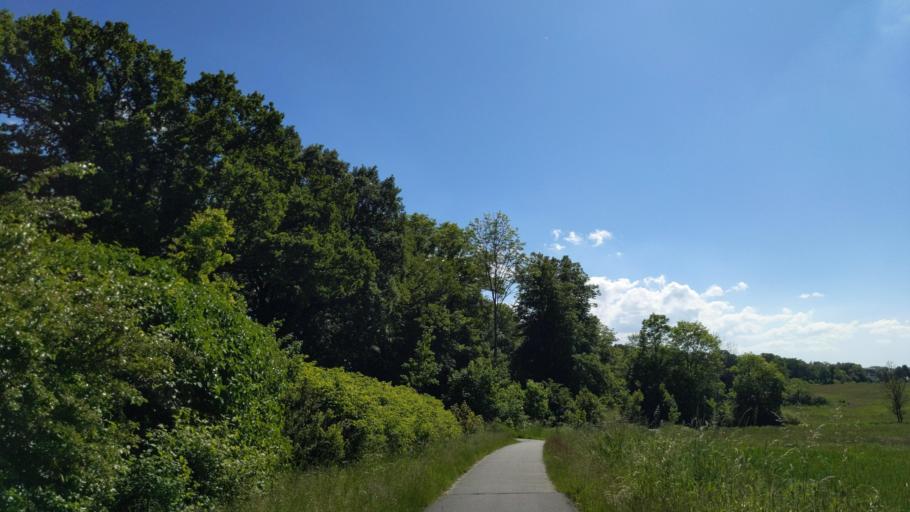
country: DE
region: Schleswig-Holstein
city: Eutin
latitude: 54.1375
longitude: 10.6421
